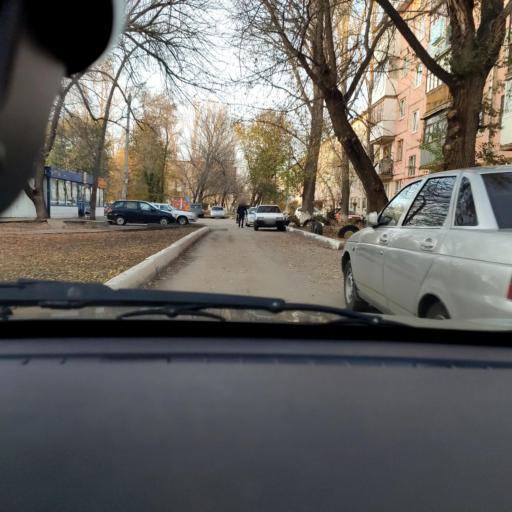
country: RU
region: Samara
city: Tol'yatti
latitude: 53.5014
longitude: 49.4084
